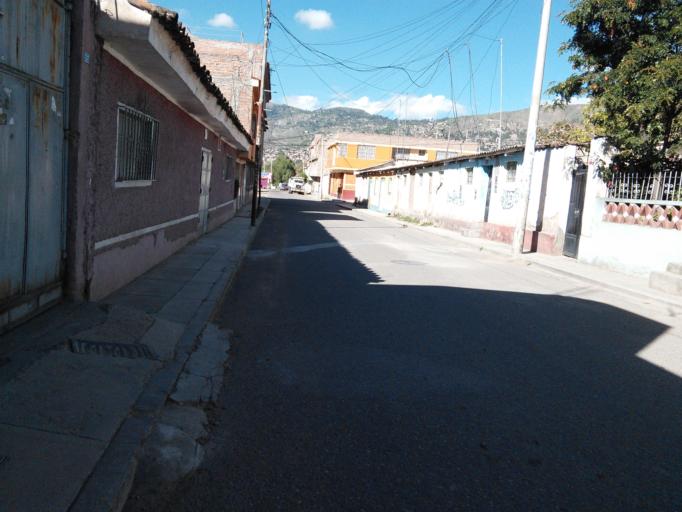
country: PE
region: Ayacucho
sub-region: Provincia de Huamanga
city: Ayacucho
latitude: -13.1546
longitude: -74.2175
